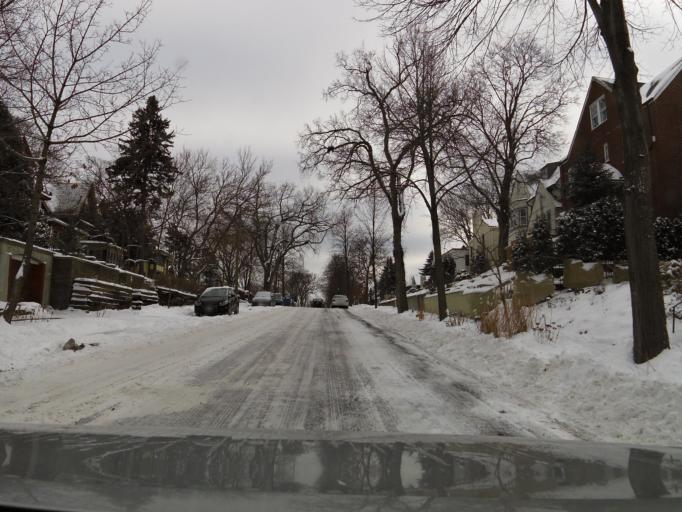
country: US
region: Minnesota
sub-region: Hennepin County
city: Saint Louis Park
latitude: 44.9411
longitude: -93.3010
